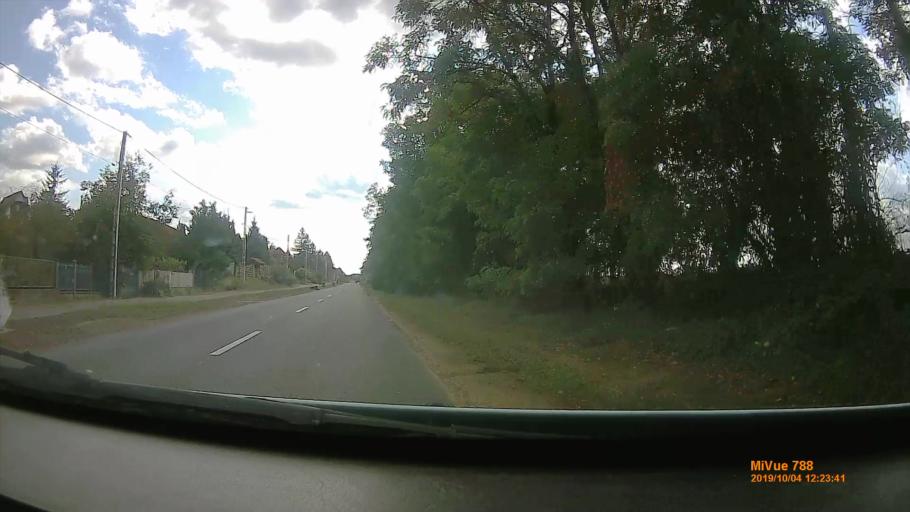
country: HU
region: Szabolcs-Szatmar-Bereg
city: Kotaj
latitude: 48.0034
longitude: 21.6988
